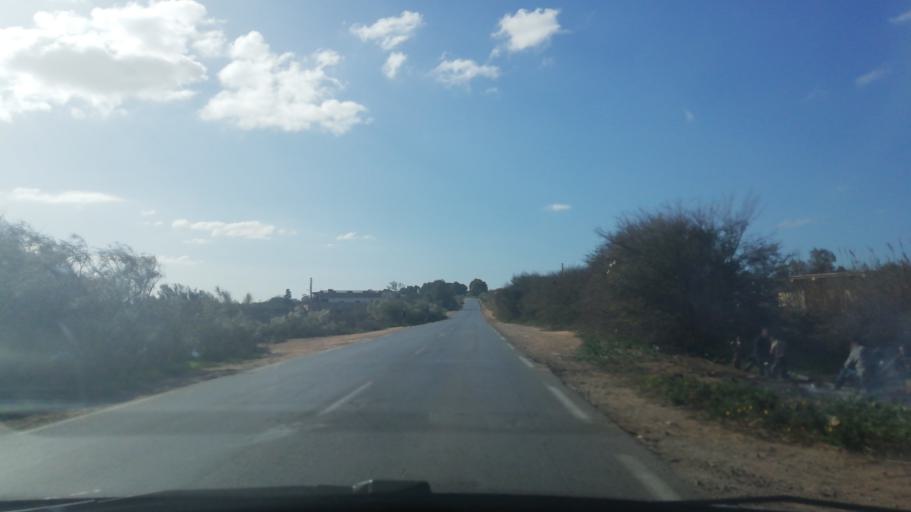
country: DZ
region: Mostaganem
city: Mostaganem
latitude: 35.9556
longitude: 0.2357
